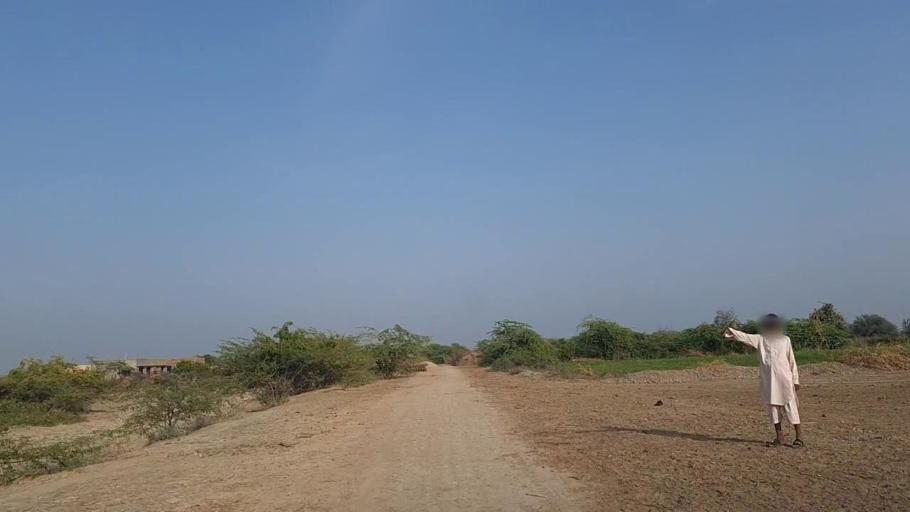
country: PK
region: Sindh
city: Dhoro Naro
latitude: 25.4971
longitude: 69.5001
